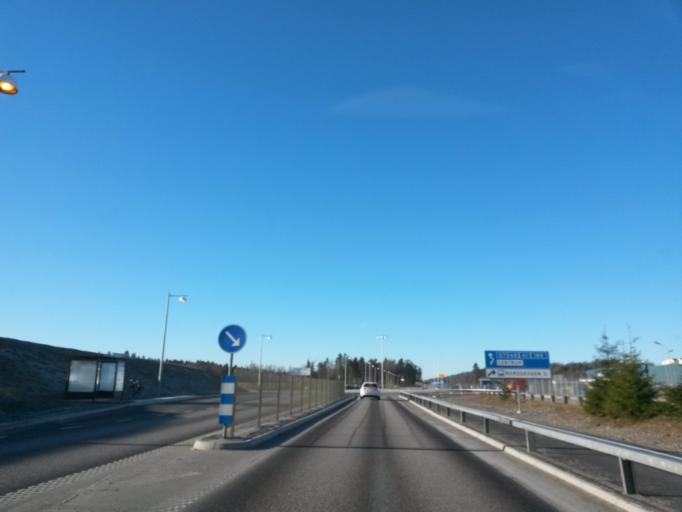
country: SE
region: Vaestra Goetaland
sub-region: Boras Kommun
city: Boras
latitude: 57.7521
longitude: 12.9581
